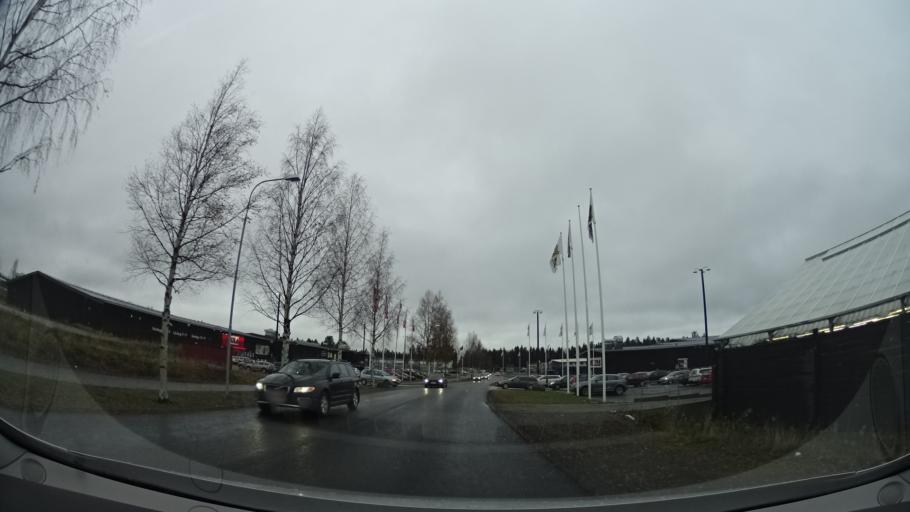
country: SE
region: Vaesterbotten
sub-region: Skelleftea Kommun
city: Skelleftea
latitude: 64.7659
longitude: 21.0200
